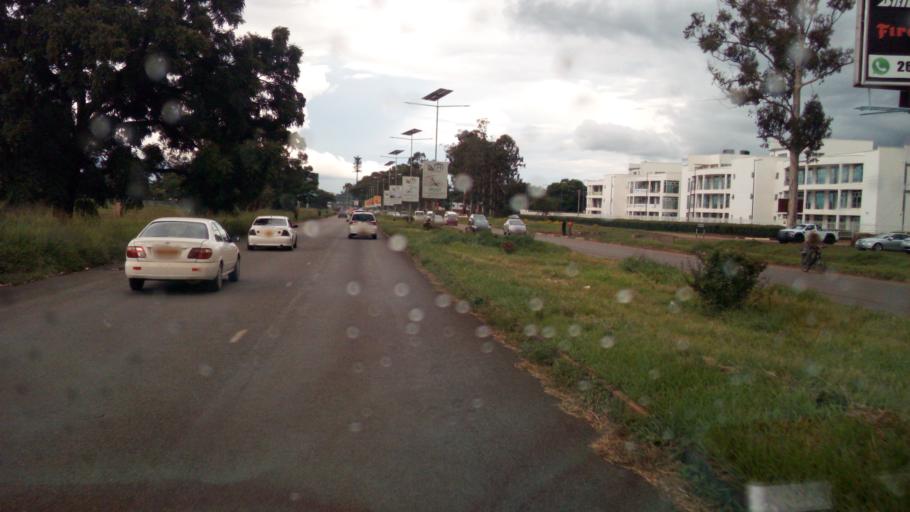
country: ZW
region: Harare
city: Harare
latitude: -17.7856
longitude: 31.0742
